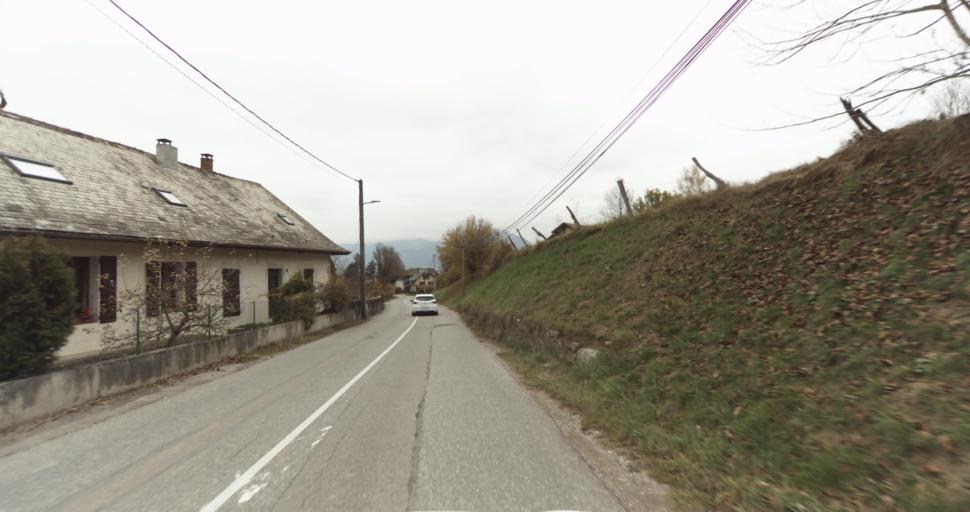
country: FR
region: Rhone-Alpes
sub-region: Departement de la Haute-Savoie
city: Saint-Jorioz
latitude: 45.8236
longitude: 6.1506
